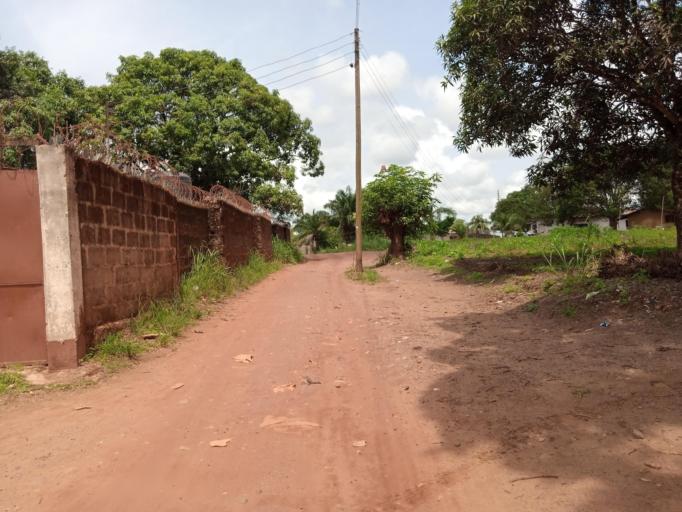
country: SL
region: Southern Province
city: Bo
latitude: 7.9461
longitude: -11.7195
